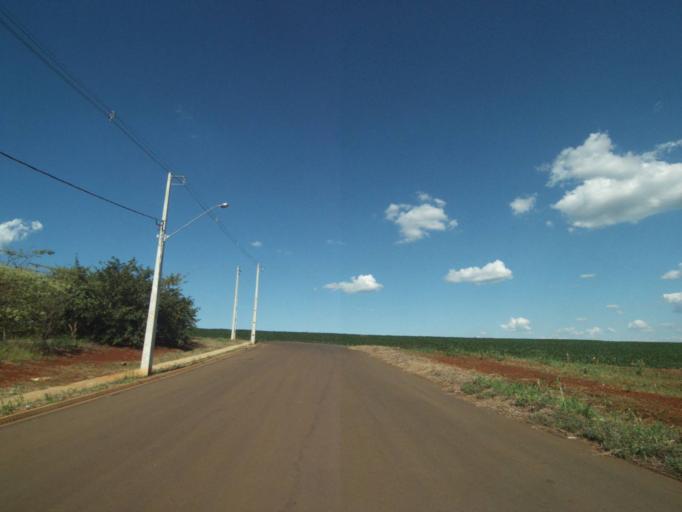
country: BR
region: Parana
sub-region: Sertanopolis
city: Sertanopolis
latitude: -23.0436
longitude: -50.8144
